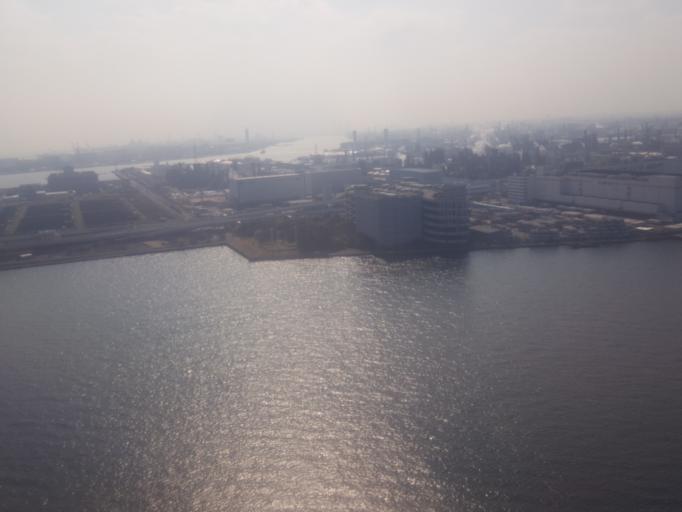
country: JP
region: Kanagawa
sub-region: Kawasaki-shi
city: Kawasaki
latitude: 35.5247
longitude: 139.7941
